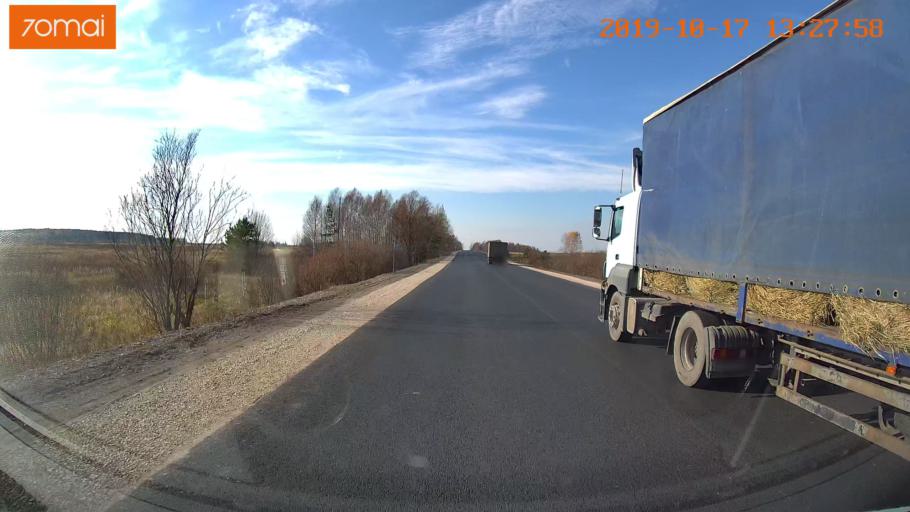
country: RU
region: Vladimir
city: Velikodvorskiy
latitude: 55.1146
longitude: 40.8819
